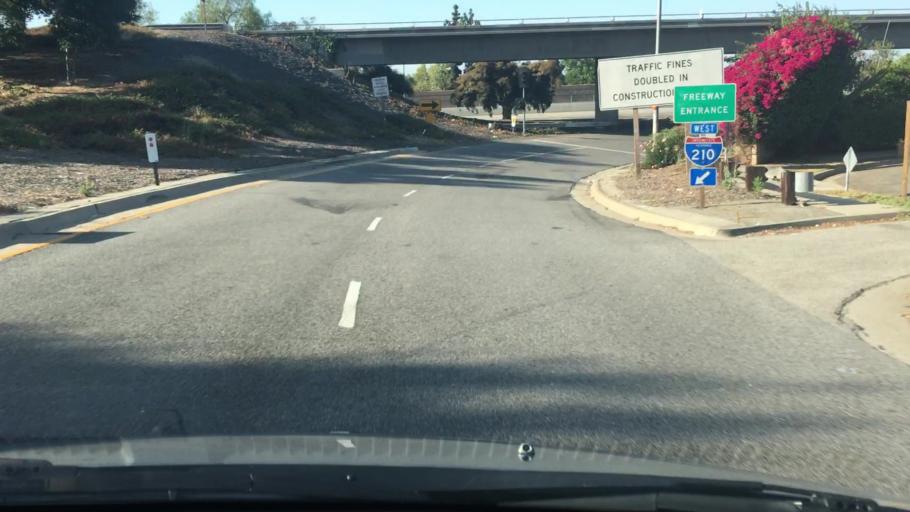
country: US
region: California
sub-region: Los Angeles County
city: Sierra Madre
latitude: 34.1497
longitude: -118.0706
